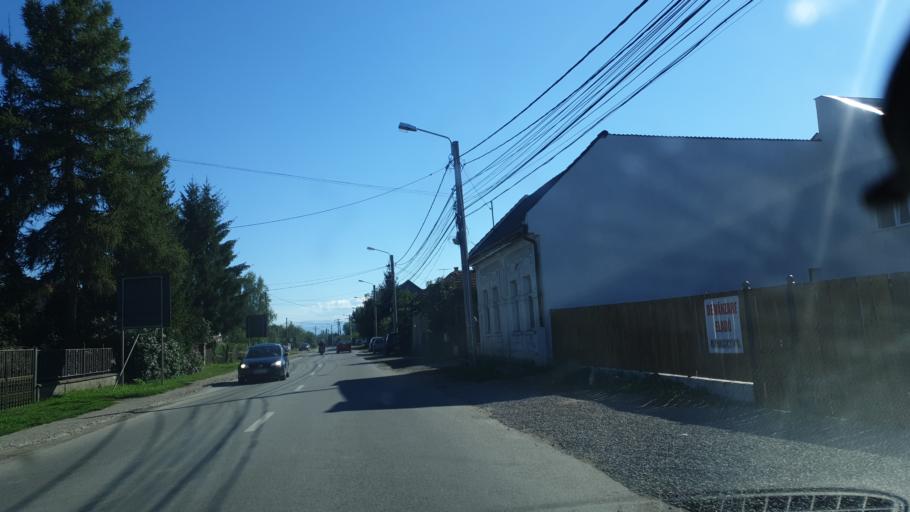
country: RO
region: Covasna
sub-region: Municipiul Sfantu Gheorghe
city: Sfantu-Gheorghe
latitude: 45.8543
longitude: 25.7783
